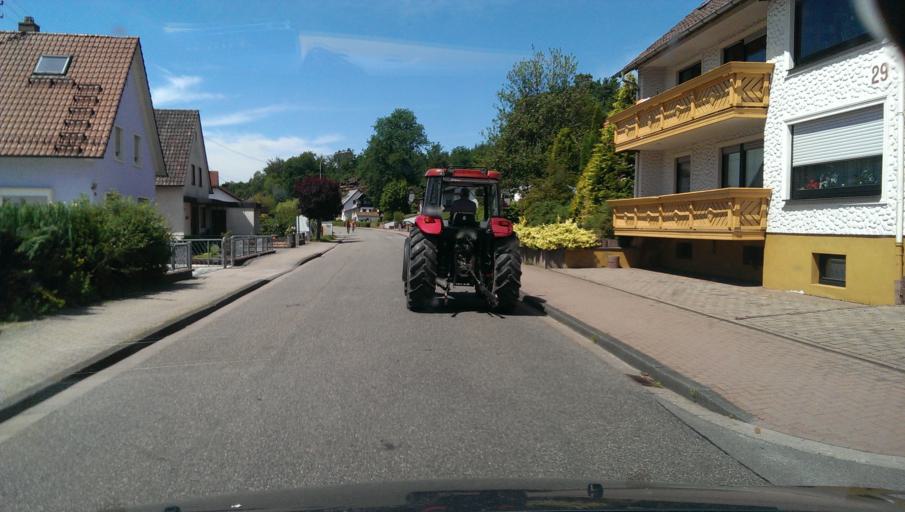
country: DE
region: Rheinland-Pfalz
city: Fischbach
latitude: 49.0879
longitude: 7.7031
